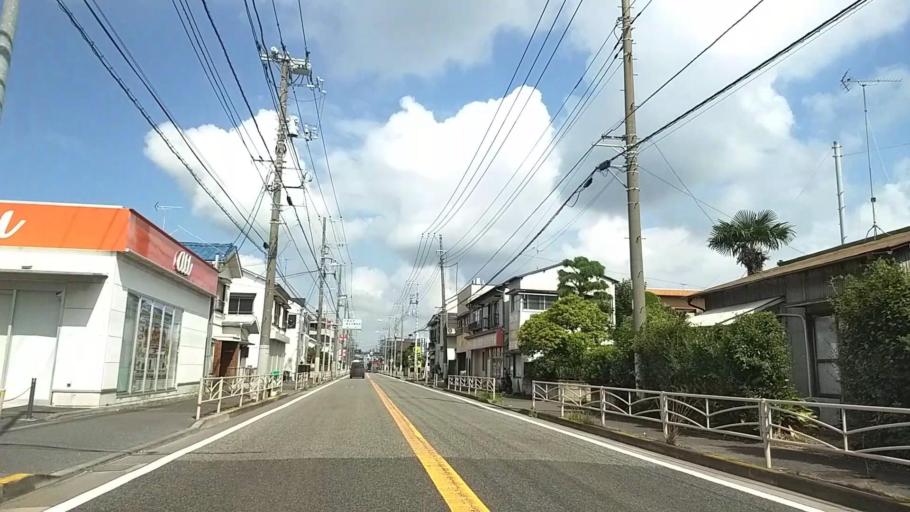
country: JP
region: Kanagawa
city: Minami-rinkan
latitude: 35.4801
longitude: 139.5358
